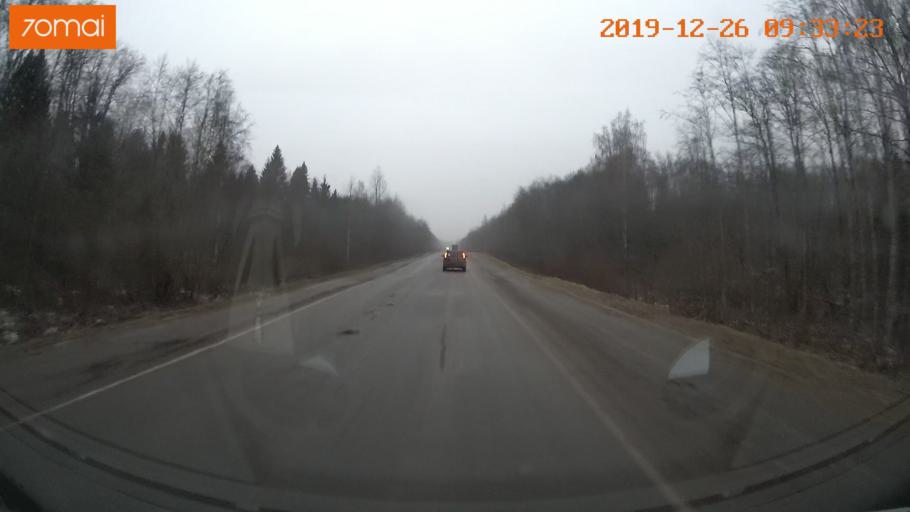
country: RU
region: Vologda
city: Vologda
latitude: 59.0892
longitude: 40.1016
